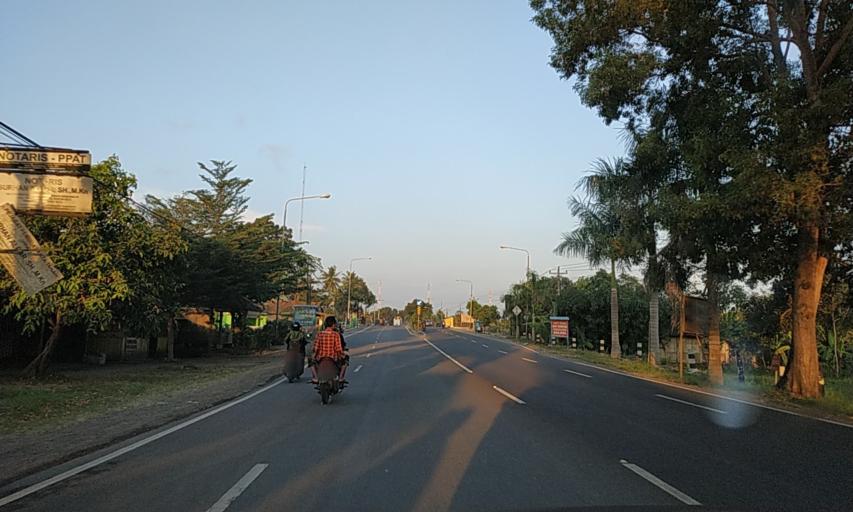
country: ID
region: Daerah Istimewa Yogyakarta
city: Srandakan
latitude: -7.8866
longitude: 110.0709
